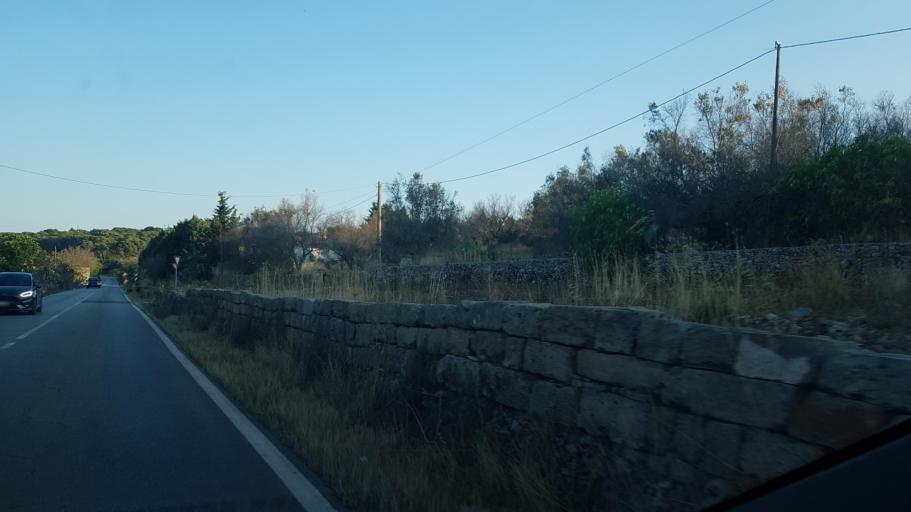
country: IT
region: Apulia
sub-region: Provincia di Lecce
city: Specchia
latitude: 39.9569
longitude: 18.2865
